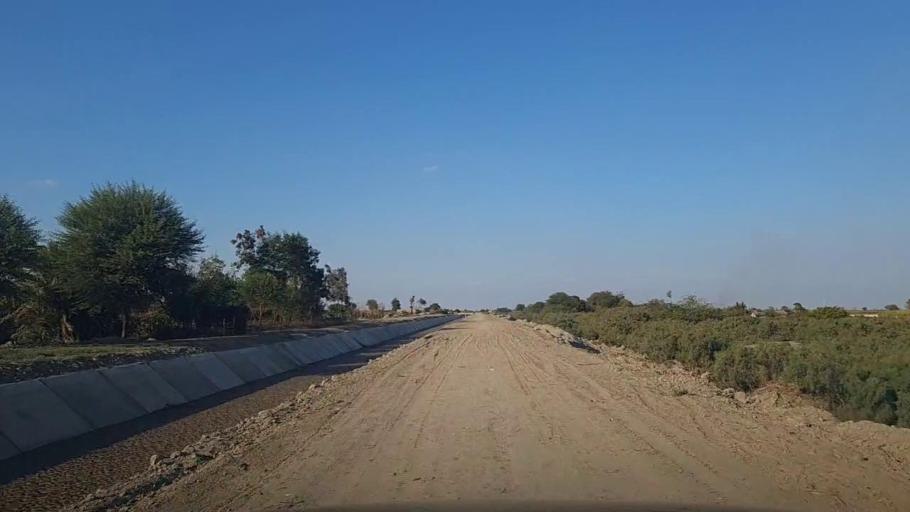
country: PK
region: Sindh
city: Jhol
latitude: 25.9156
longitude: 69.0407
